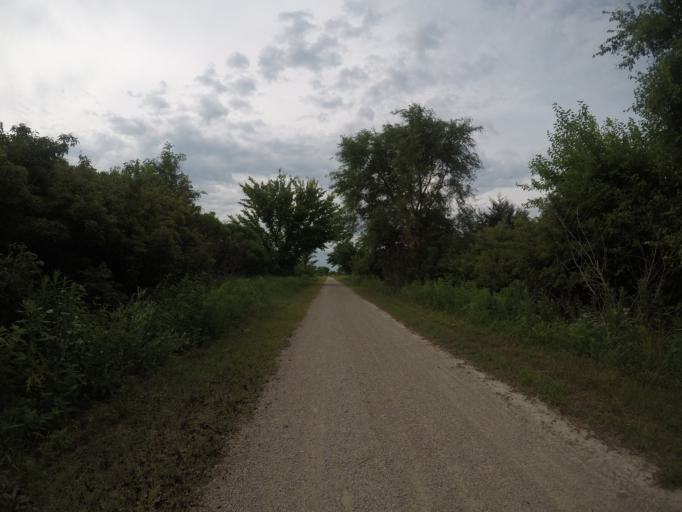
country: US
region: Kansas
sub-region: Franklin County
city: Ottawa
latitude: 38.4612
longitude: -95.2703
